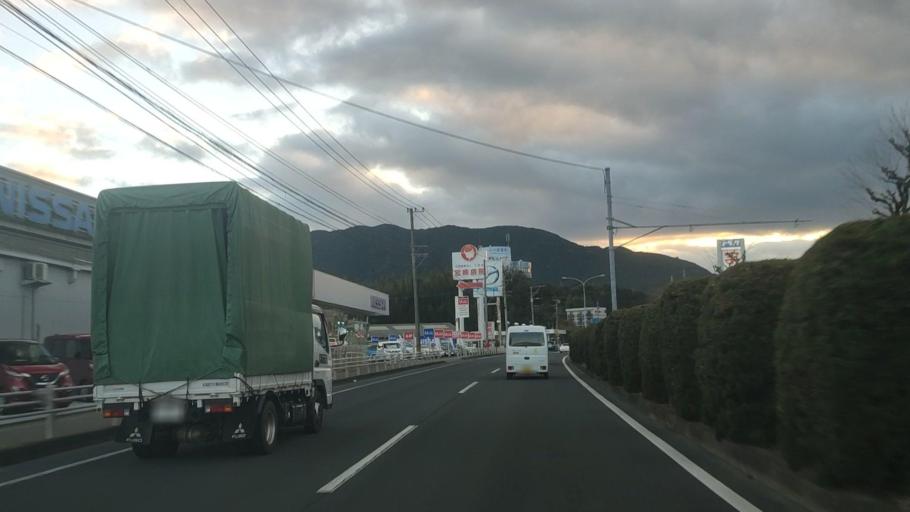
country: JP
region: Nagasaki
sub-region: Isahaya-shi
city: Isahaya
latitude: 32.8321
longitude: 130.0015
